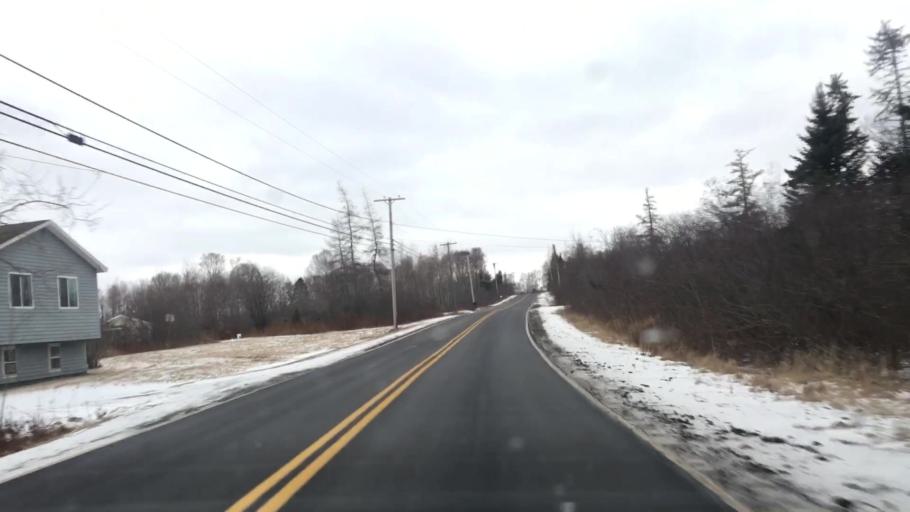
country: US
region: Maine
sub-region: Washington County
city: Machiasport
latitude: 44.7018
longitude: -67.3460
